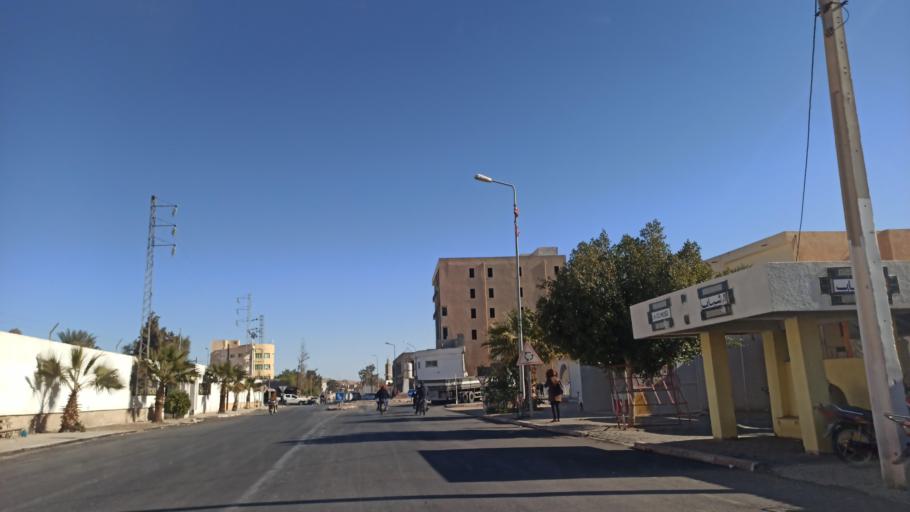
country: TN
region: Gafsa
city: Al Metlaoui
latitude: 34.3136
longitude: 8.3894
